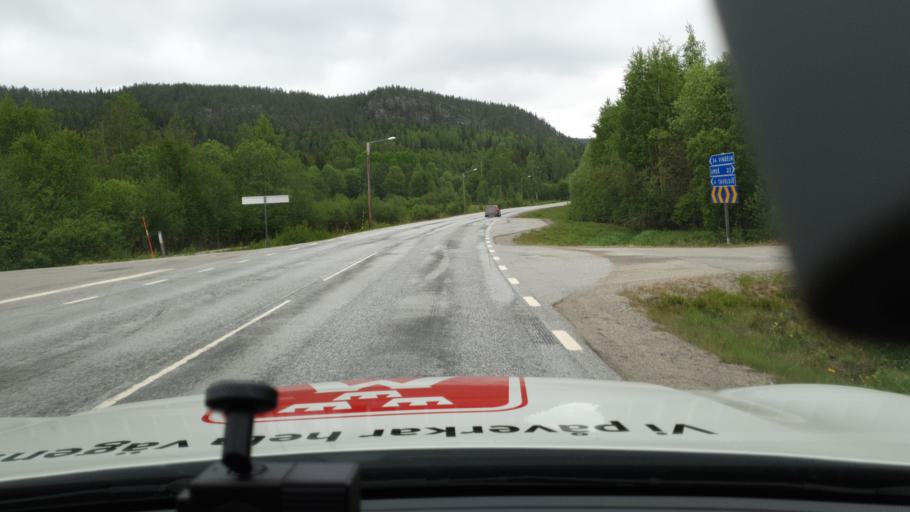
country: SE
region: Vaesterbotten
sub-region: Vannas Kommun
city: Vannasby
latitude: 63.9930
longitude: 20.0406
